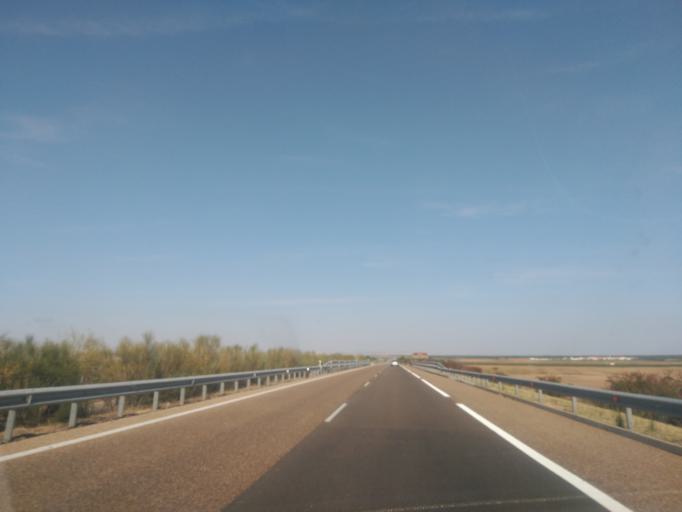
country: ES
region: Castille and Leon
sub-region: Provincia de Valladolid
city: Pollos
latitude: 41.4190
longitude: -5.1203
